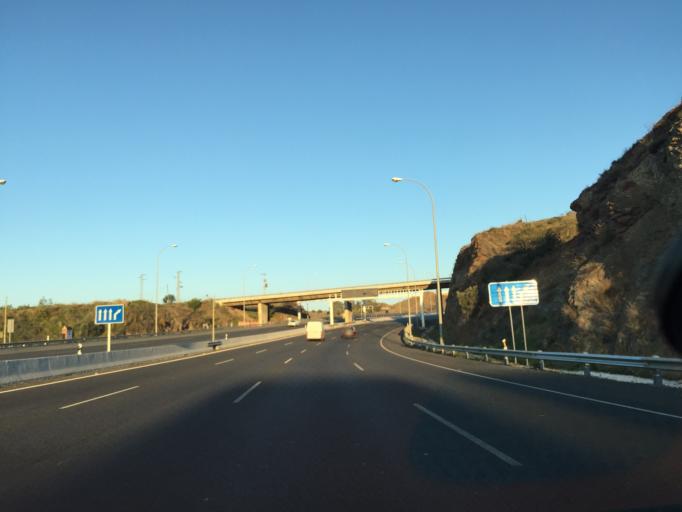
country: ES
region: Andalusia
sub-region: Provincia de Malaga
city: Malaga
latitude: 36.7399
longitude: -4.3984
